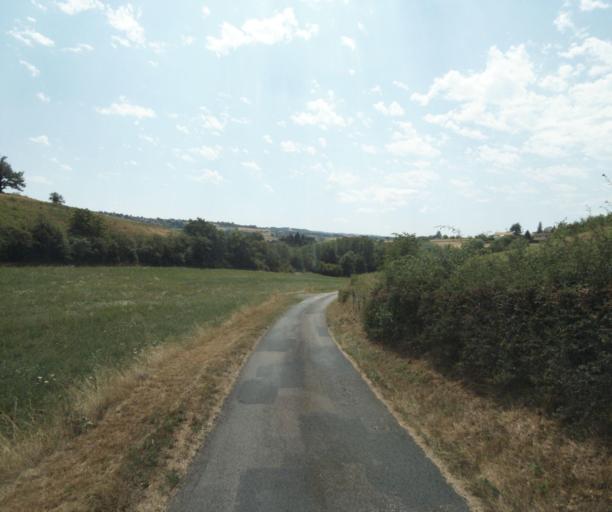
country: FR
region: Rhone-Alpes
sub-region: Departement du Rhone
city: Saint-Germain-Nuelles
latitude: 45.8498
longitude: 4.6309
